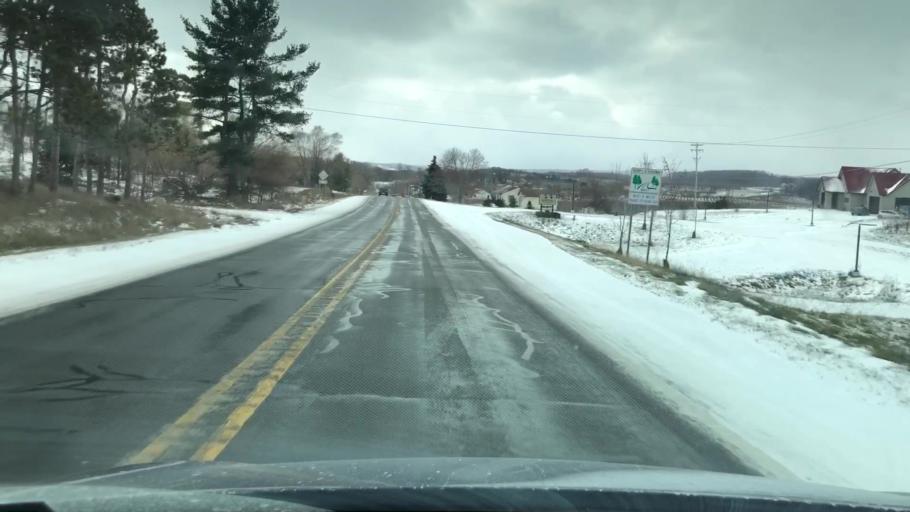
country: US
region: Michigan
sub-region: Antrim County
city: Elk Rapids
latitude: 44.8611
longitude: -85.5214
